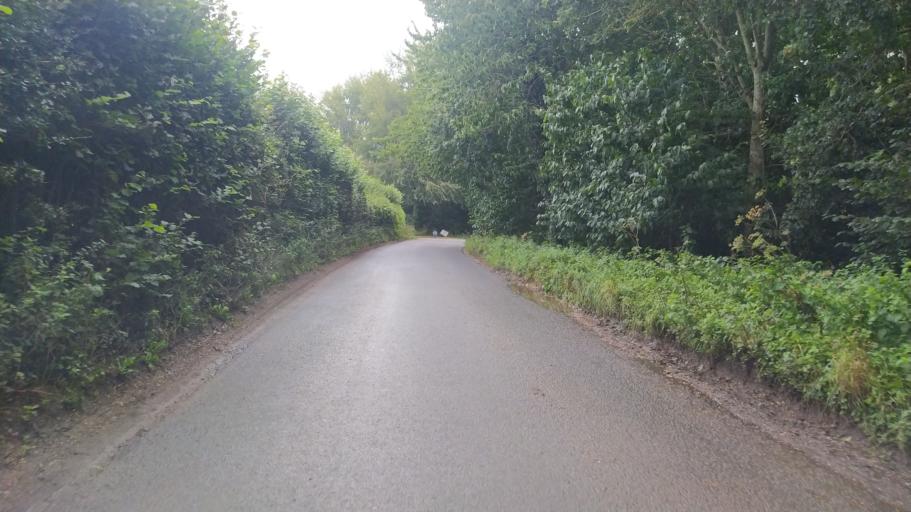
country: GB
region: England
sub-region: Dorset
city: Verwood
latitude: 50.9172
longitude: -1.9108
